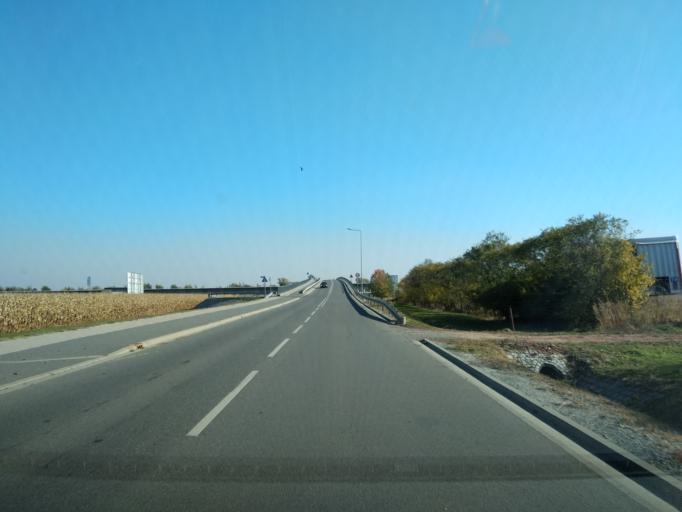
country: PL
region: Lower Silesian Voivodeship
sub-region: Powiat wroclawski
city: Smolec
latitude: 51.0745
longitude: 16.9237
